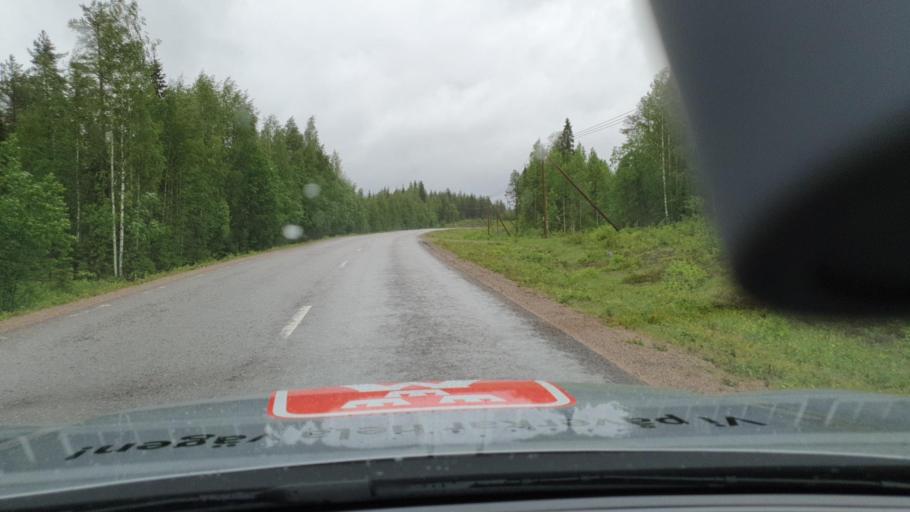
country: SE
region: Norrbotten
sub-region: Overkalix Kommun
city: OEverkalix
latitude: 66.4434
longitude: 23.0406
